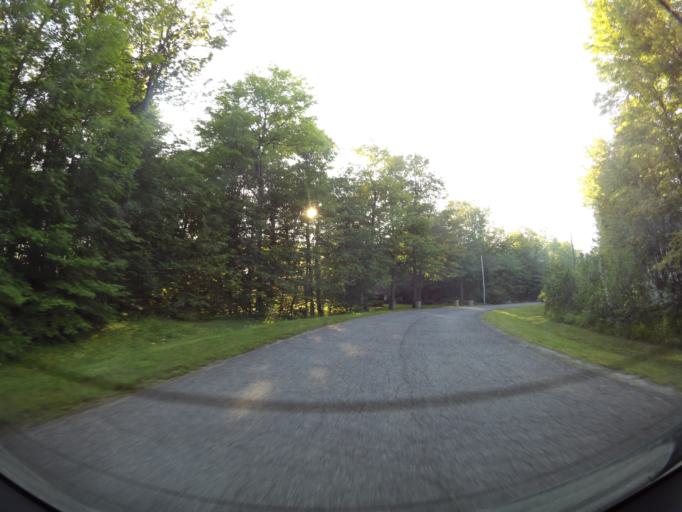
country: CA
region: Ontario
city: Clarence-Rockland
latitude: 45.5029
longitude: -75.4059
